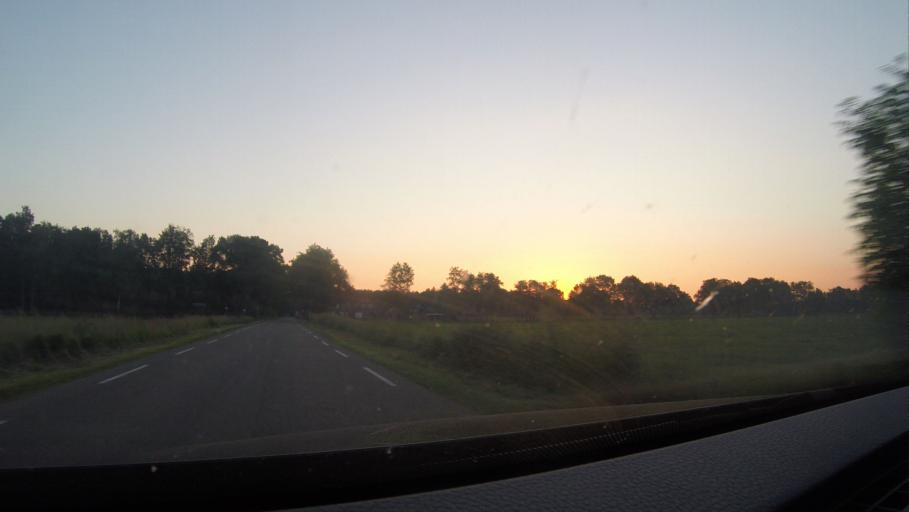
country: NL
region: Overijssel
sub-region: Gemeente Raalte
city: Raalte
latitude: 52.3138
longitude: 6.2787
